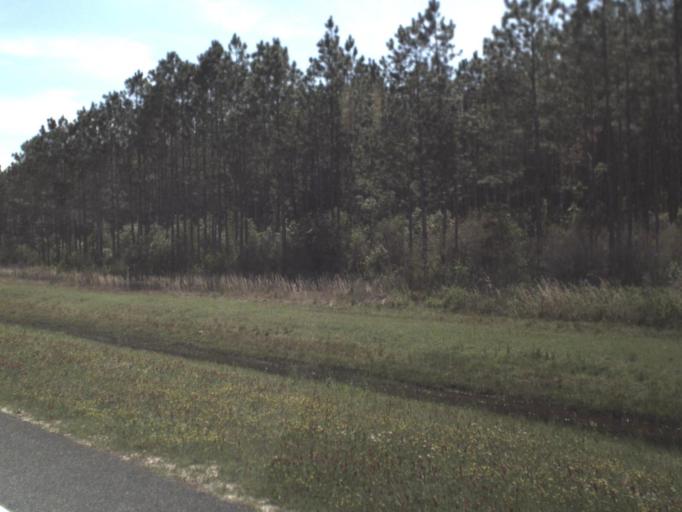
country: US
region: Florida
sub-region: Bay County
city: Lynn Haven
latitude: 30.3407
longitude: -85.6607
